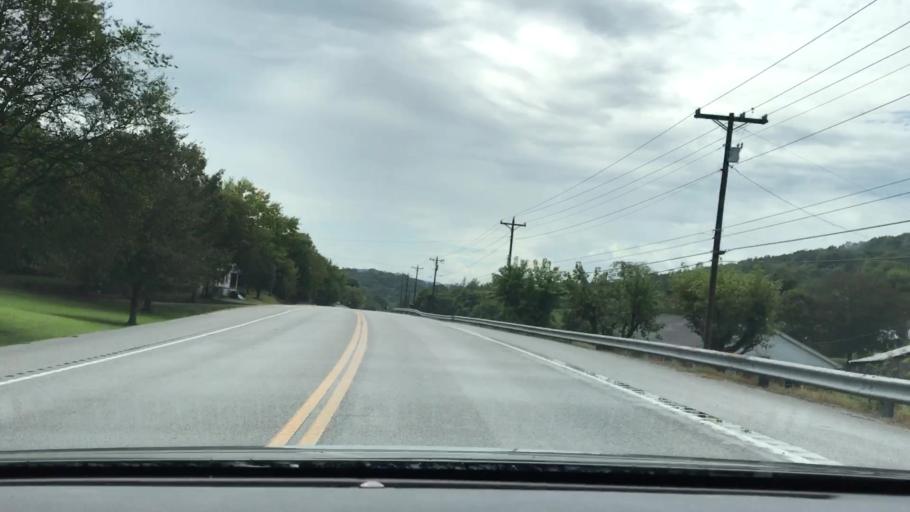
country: US
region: Tennessee
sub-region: Smith County
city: Carthage
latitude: 36.3003
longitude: -85.9790
